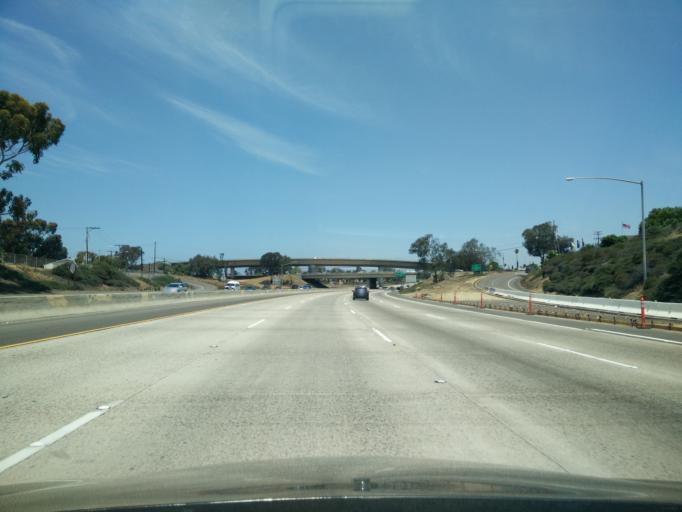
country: US
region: California
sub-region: San Diego County
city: Imperial Beach
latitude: 32.5812
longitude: -117.0865
